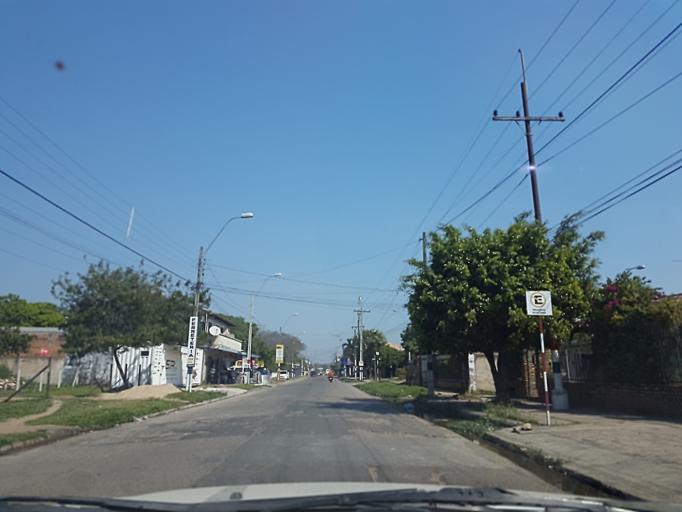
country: PY
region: Central
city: Colonia Mariano Roque Alonso
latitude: -25.2048
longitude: -57.5327
